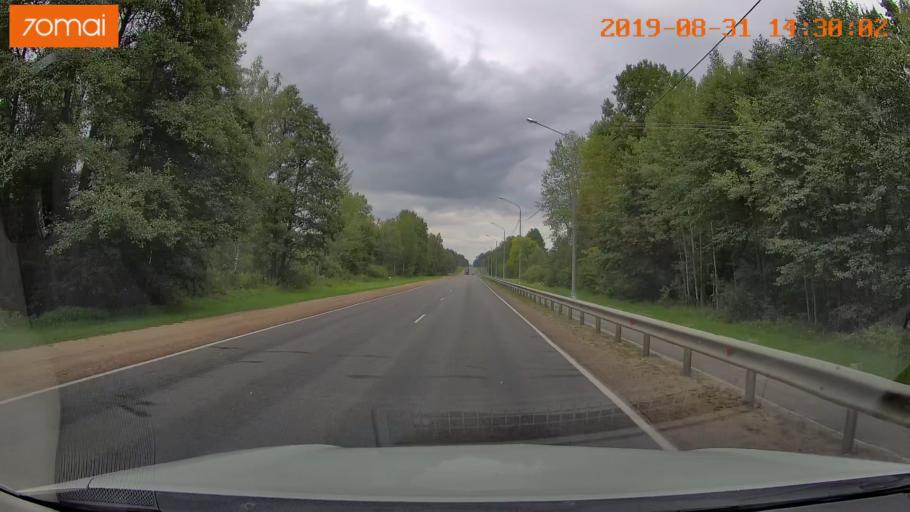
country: RU
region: Smolensk
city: Yekimovichi
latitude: 54.1292
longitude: 33.3432
